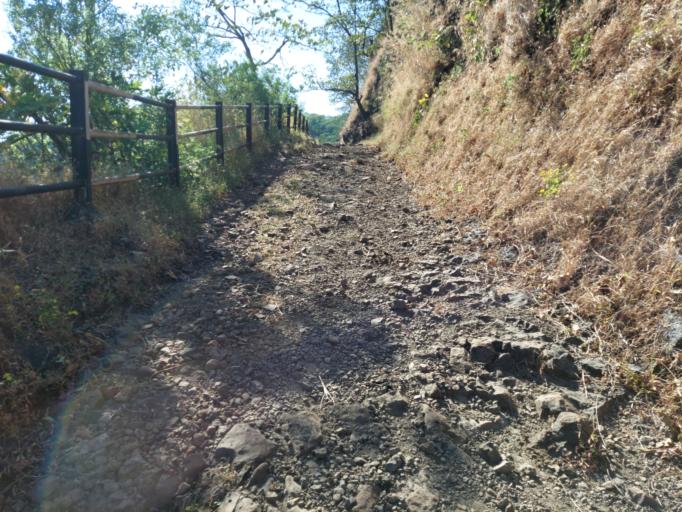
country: IN
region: Maharashtra
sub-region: Sindhudurg
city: Kudal
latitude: 16.0855
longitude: 73.8434
